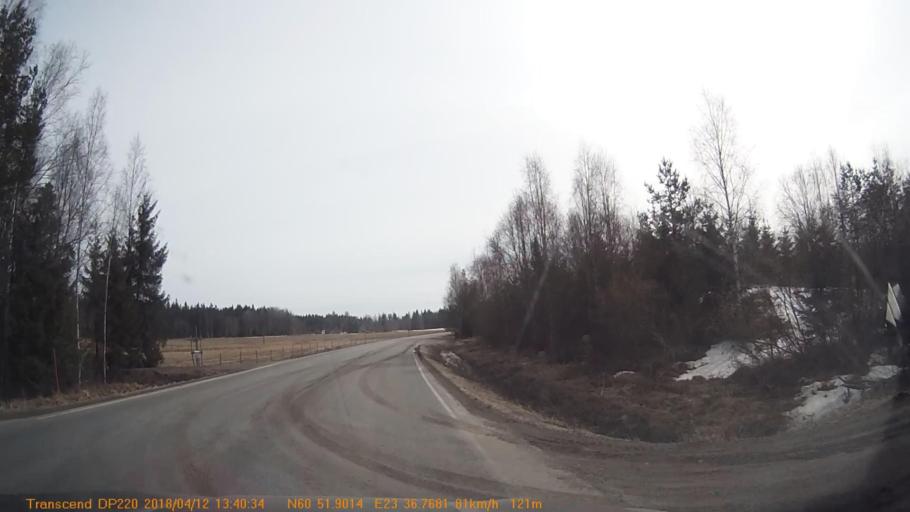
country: FI
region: Haeme
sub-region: Forssa
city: Forssa
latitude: 60.8644
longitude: 23.6133
